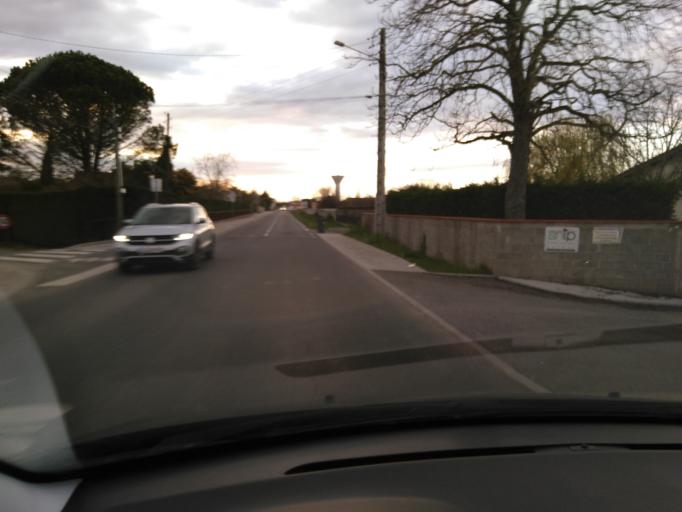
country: FR
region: Midi-Pyrenees
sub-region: Departement de la Haute-Garonne
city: Pibrac
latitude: 43.6081
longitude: 1.2682
